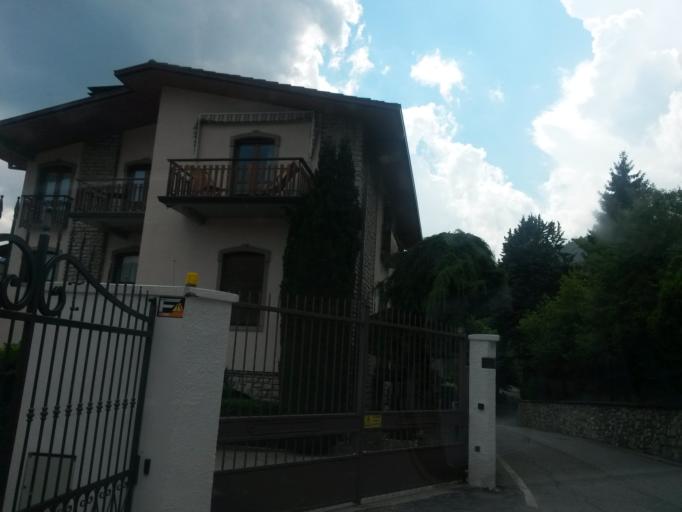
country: IT
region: Lombardy
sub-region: Provincia di Brescia
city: Gardola
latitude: 45.7406
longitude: 10.7200
